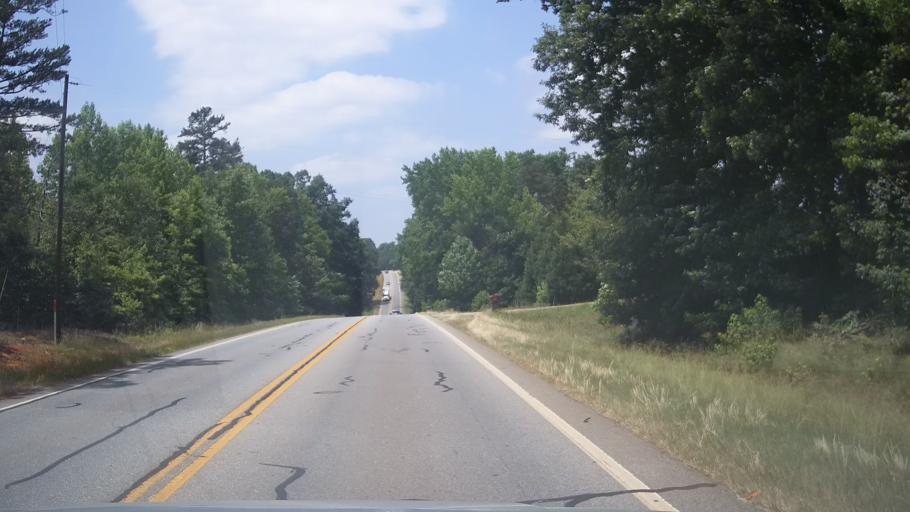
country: US
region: Georgia
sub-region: Jackson County
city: Commerce
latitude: 34.1921
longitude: -83.4121
